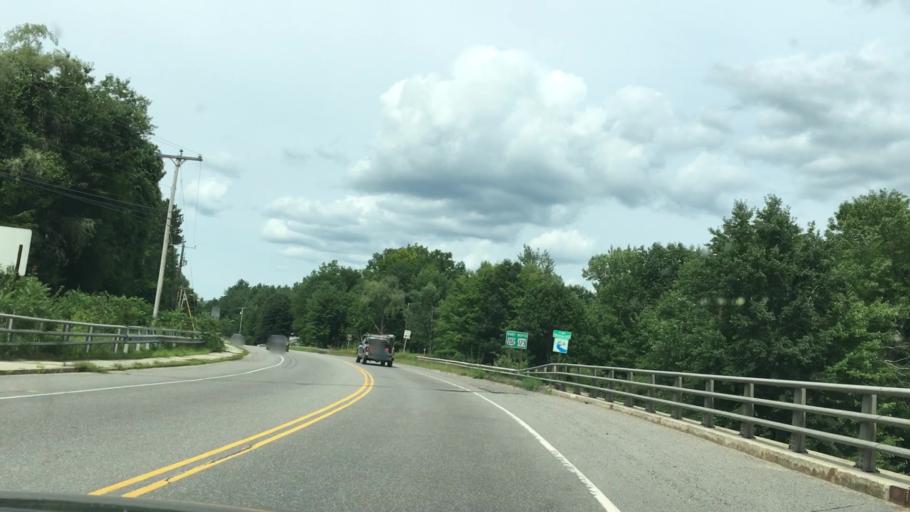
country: US
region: New Hampshire
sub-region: Hillsborough County
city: Peterborough
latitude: 42.8994
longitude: -71.9386
